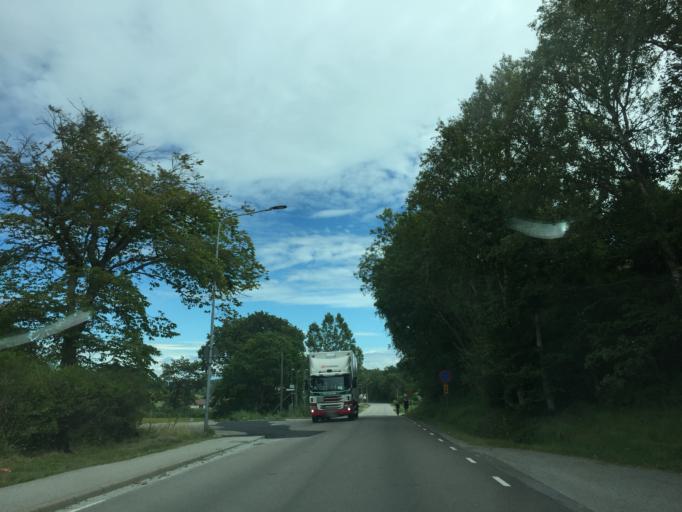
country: SE
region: Vaestra Goetaland
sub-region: Tjorns Kommun
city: Skaerhamn
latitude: 57.9965
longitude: 11.5651
